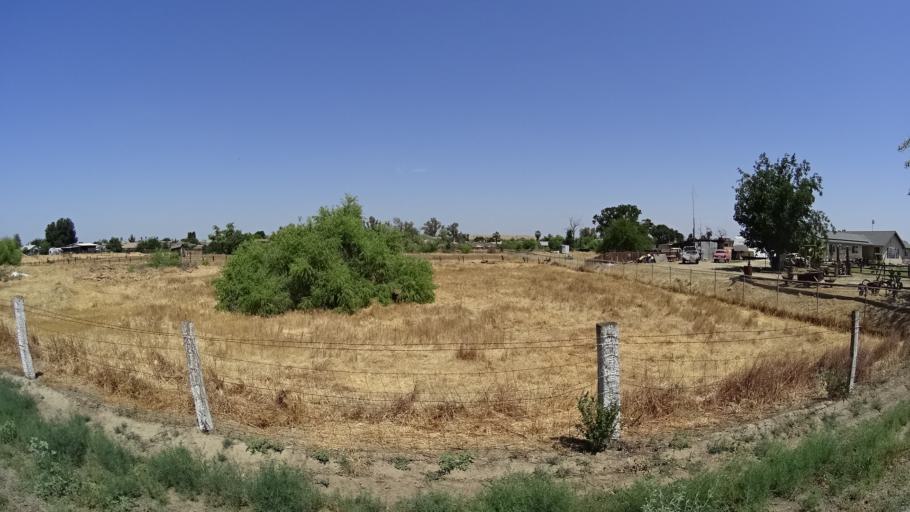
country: US
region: California
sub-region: Kings County
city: Armona
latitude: 36.3057
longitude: -119.7063
